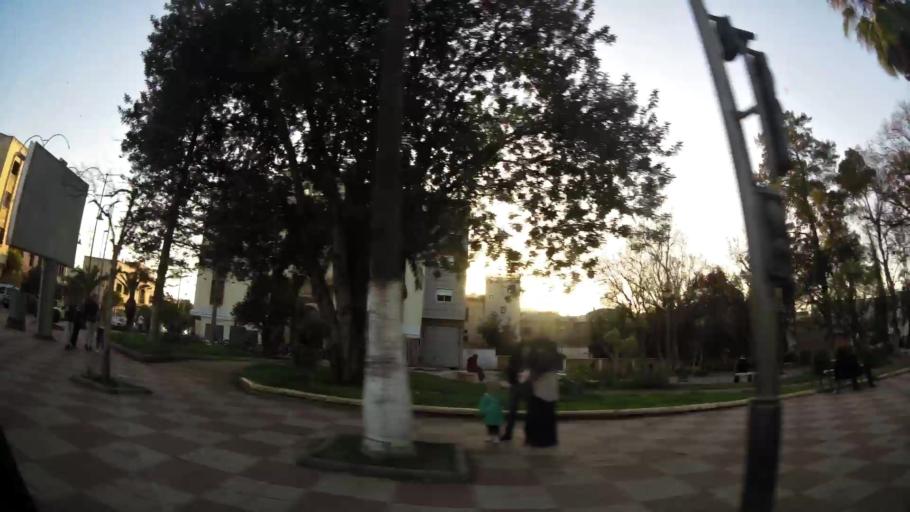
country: MA
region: Chaouia-Ouardigha
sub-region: Settat Province
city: Settat
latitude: 33.0009
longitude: -7.6201
